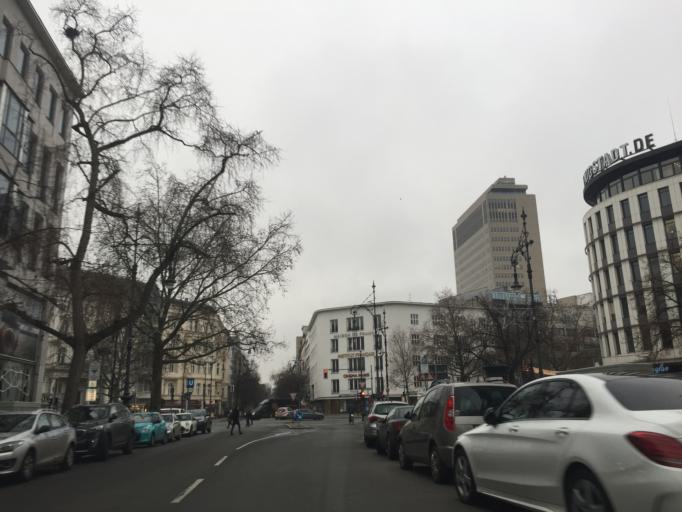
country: DE
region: Berlin
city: Wilmersdorf Bezirk
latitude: 52.5033
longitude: 13.3254
